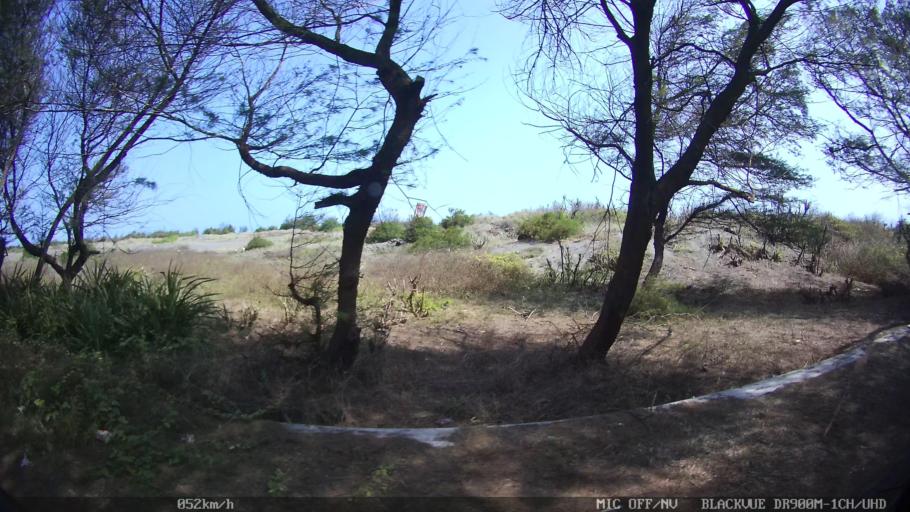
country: ID
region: Daerah Istimewa Yogyakarta
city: Bambanglipuro
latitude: -8.0145
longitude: 110.2982
